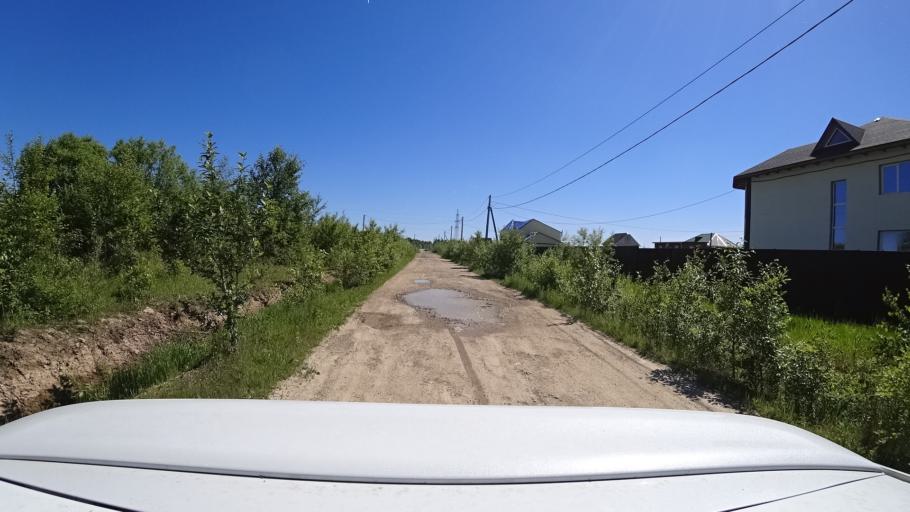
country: RU
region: Khabarovsk Krai
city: Topolevo
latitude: 48.5648
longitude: 135.1927
